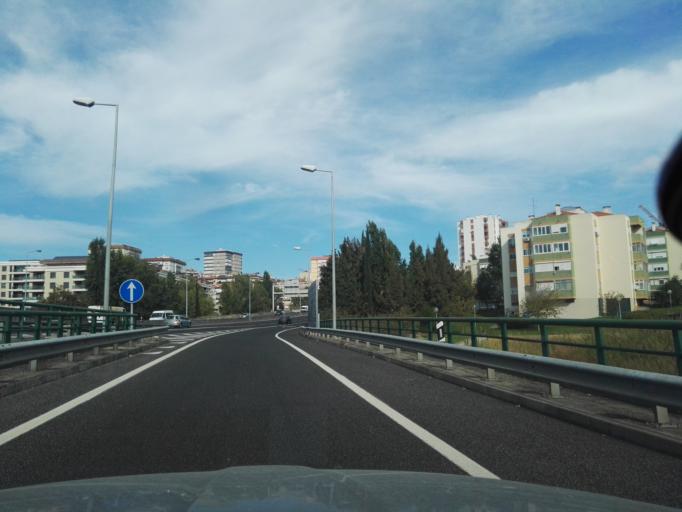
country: PT
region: Lisbon
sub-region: Odivelas
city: Olival do Basto
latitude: 38.7925
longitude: -9.1706
